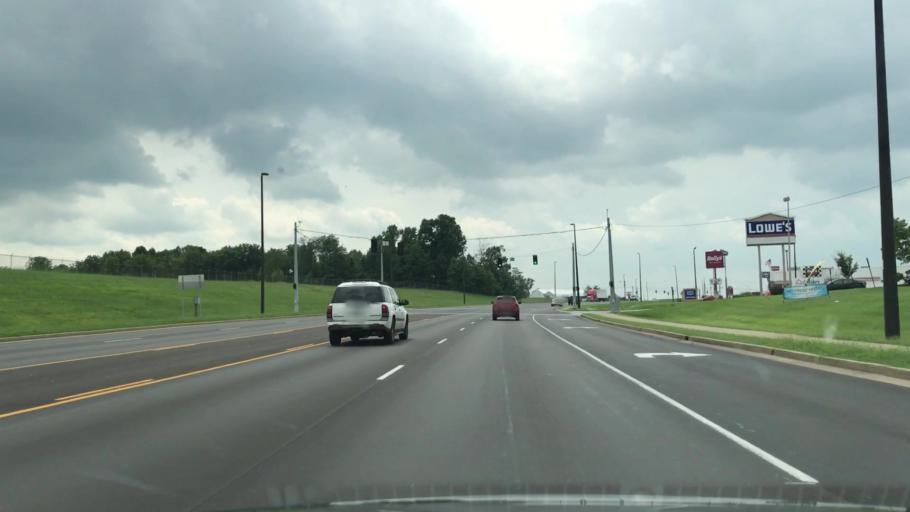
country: US
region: Kentucky
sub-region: Barren County
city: Glasgow
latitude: 36.9994
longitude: -85.9279
